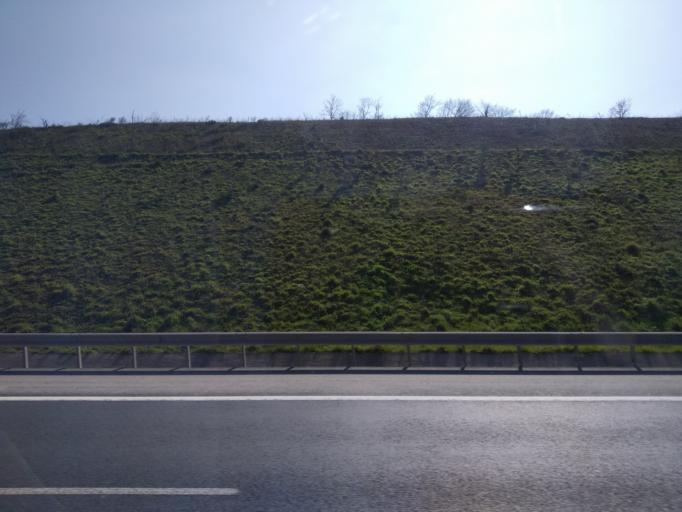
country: TR
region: Istanbul
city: Kemerburgaz
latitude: 41.2297
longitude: 28.8618
